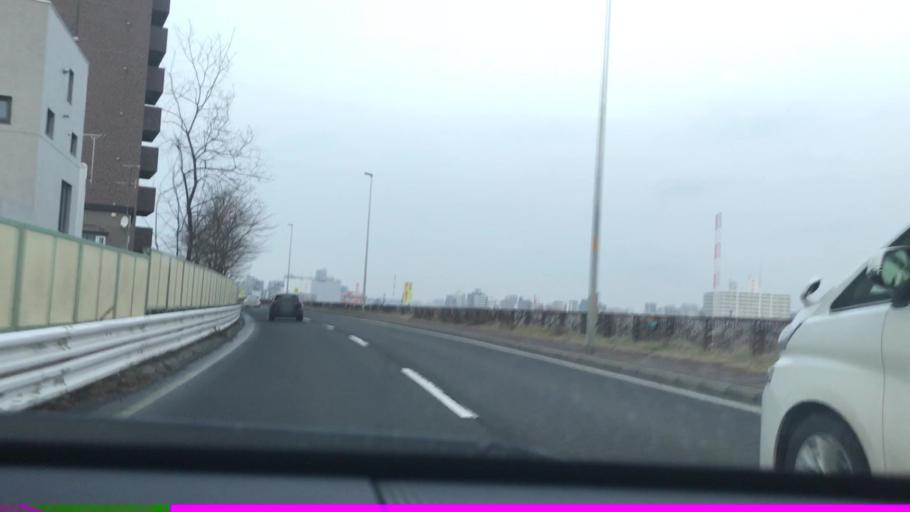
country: JP
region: Hokkaido
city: Sapporo
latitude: 43.0239
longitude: 141.3515
